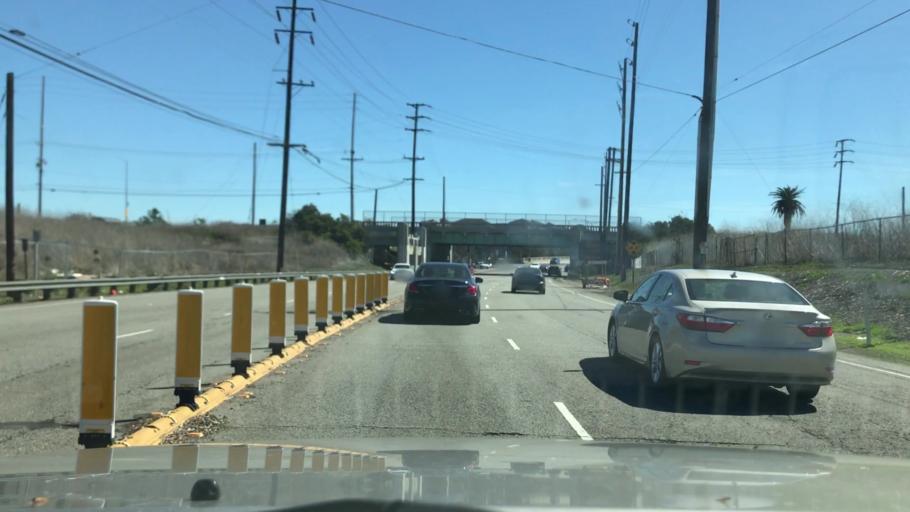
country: US
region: California
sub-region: Los Angeles County
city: Marina del Rey
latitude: 33.9768
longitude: -118.4341
